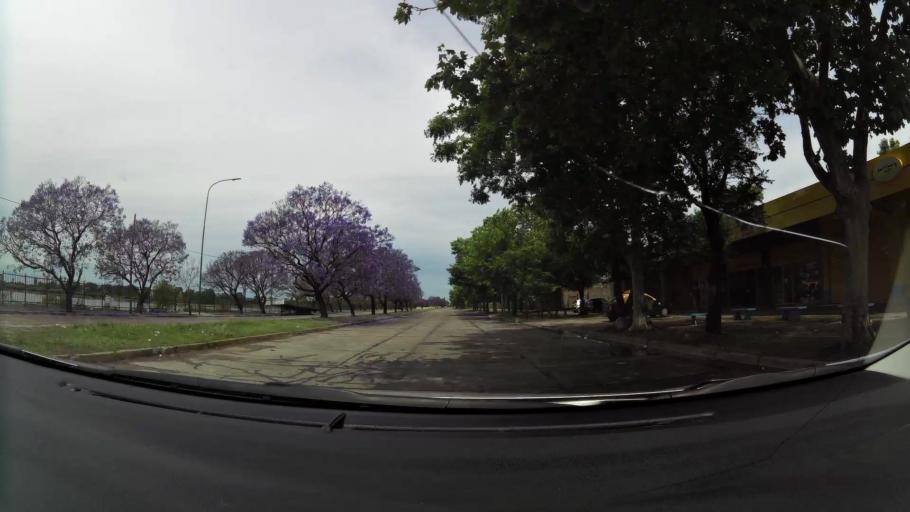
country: AR
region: Buenos Aires F.D.
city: Villa Lugano
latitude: -34.6813
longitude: -58.4489
